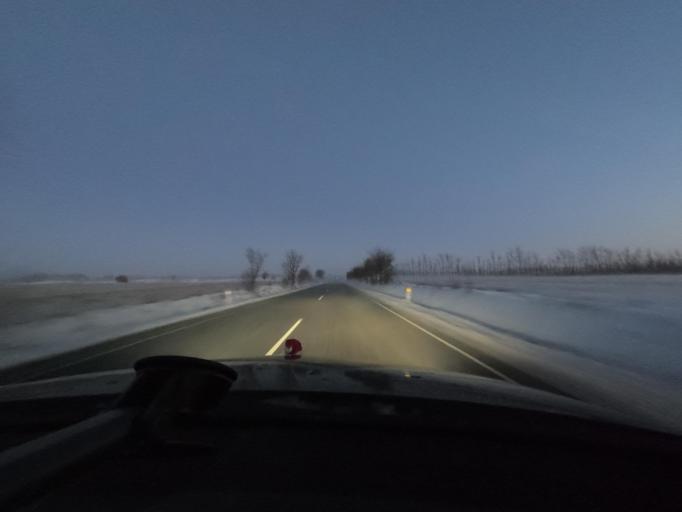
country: DK
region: South Denmark
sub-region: Tonder Kommune
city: Sherrebek
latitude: 55.1769
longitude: 8.8202
